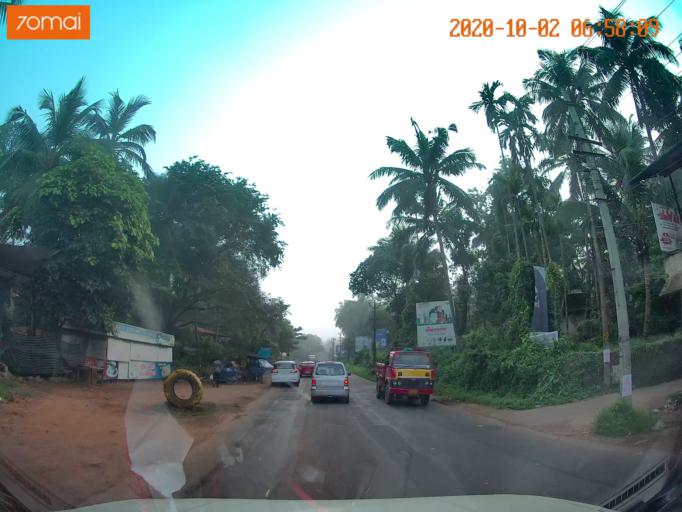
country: IN
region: Kerala
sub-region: Malappuram
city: Tirur
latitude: 10.8720
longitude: 76.0575
